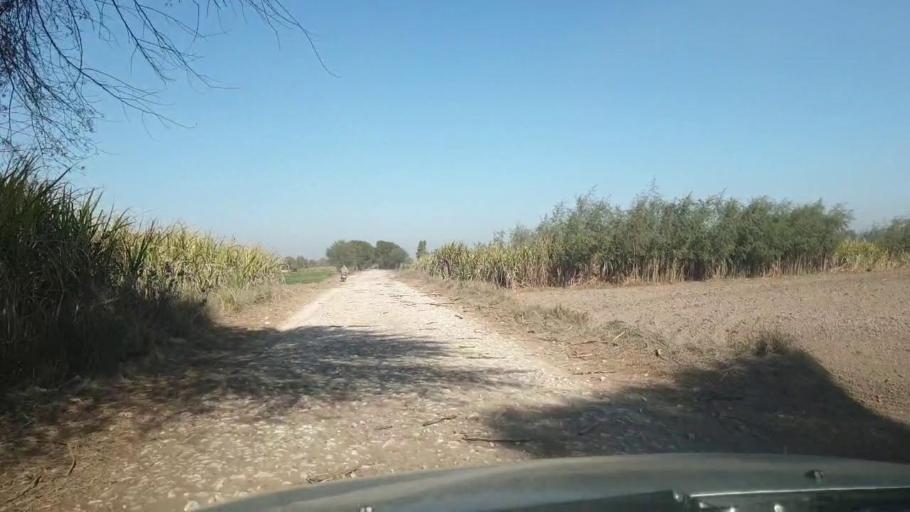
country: PK
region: Sindh
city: Ghotki
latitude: 28.0896
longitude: 69.3437
